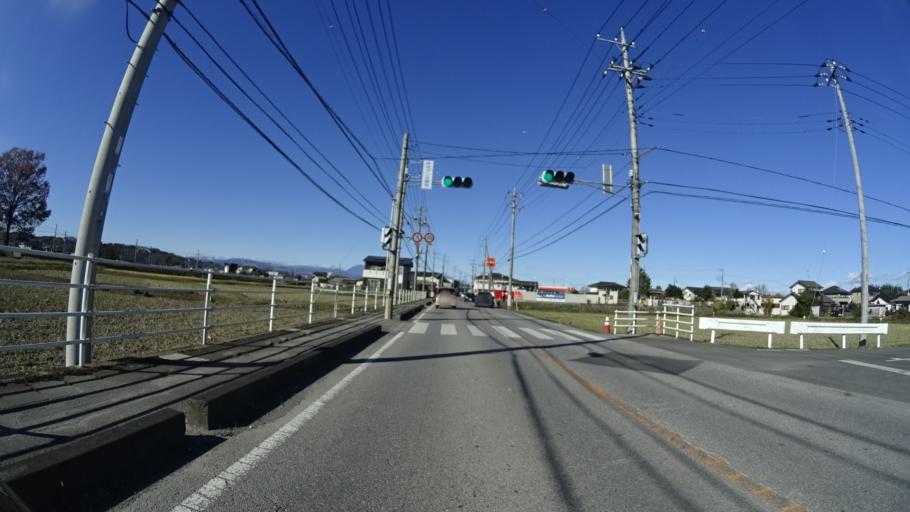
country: JP
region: Tochigi
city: Mibu
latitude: 36.4621
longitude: 139.7526
